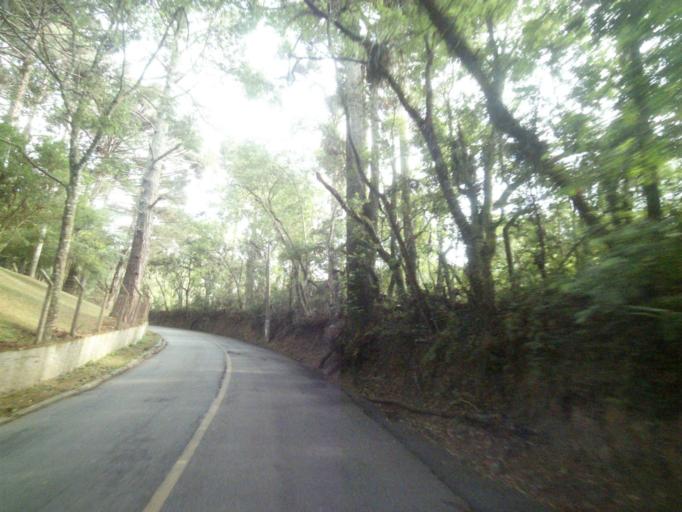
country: BR
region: Parana
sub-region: Curitiba
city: Curitiba
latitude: -25.4207
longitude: -49.3140
